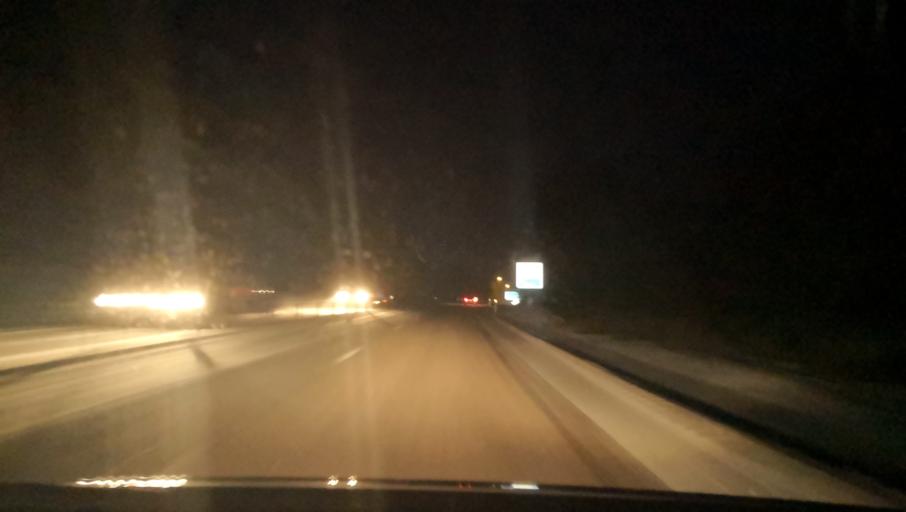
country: SE
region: Uppsala
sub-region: Heby Kommun
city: Tarnsjo
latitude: 60.2404
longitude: 16.9591
